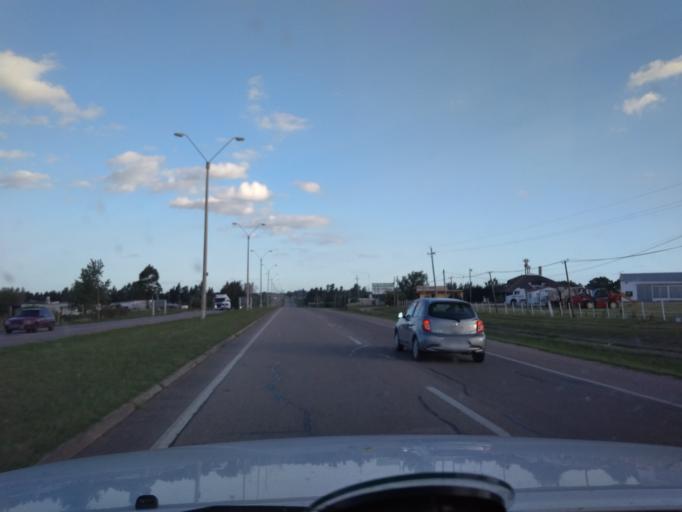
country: UY
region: Canelones
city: Joanico
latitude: -34.6146
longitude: -56.2599
